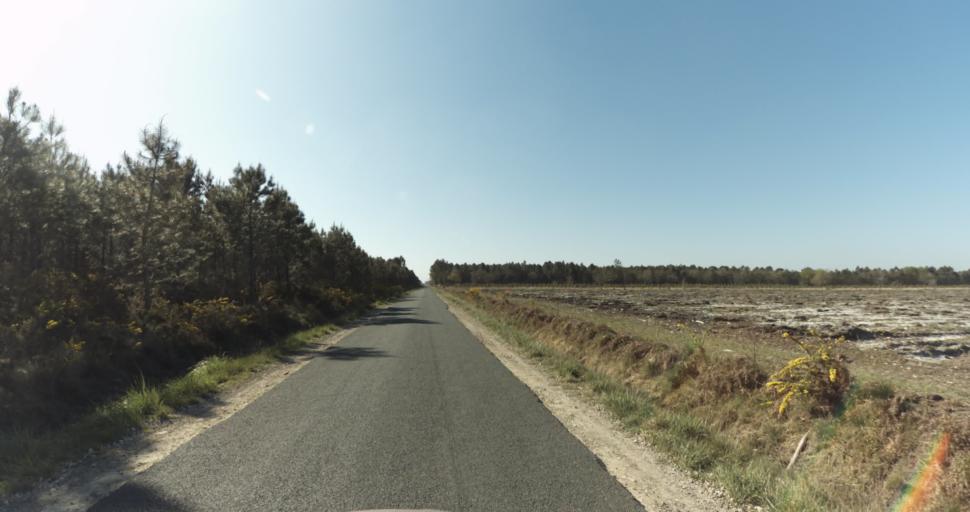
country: FR
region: Aquitaine
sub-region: Departement de la Gironde
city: Marcheprime
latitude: 44.7898
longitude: -0.8638
